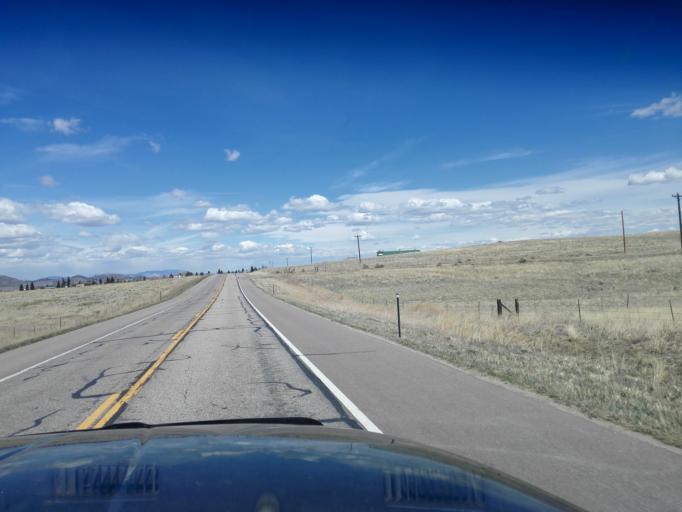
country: US
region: Colorado
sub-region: Custer County
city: Westcliffe
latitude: 38.1209
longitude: -105.4618
